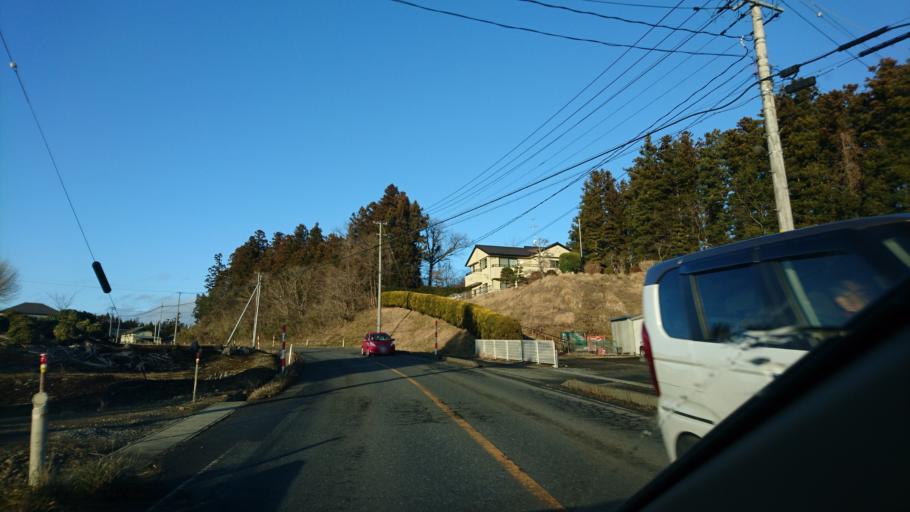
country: JP
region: Miyagi
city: Furukawa
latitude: 38.6223
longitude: 140.8734
